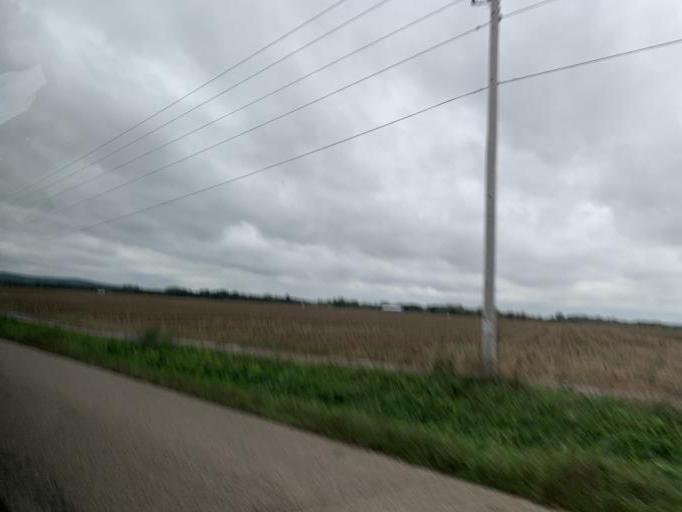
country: US
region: Wisconsin
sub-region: Sauk County
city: Prairie du Sac
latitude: 43.3351
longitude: -89.7687
